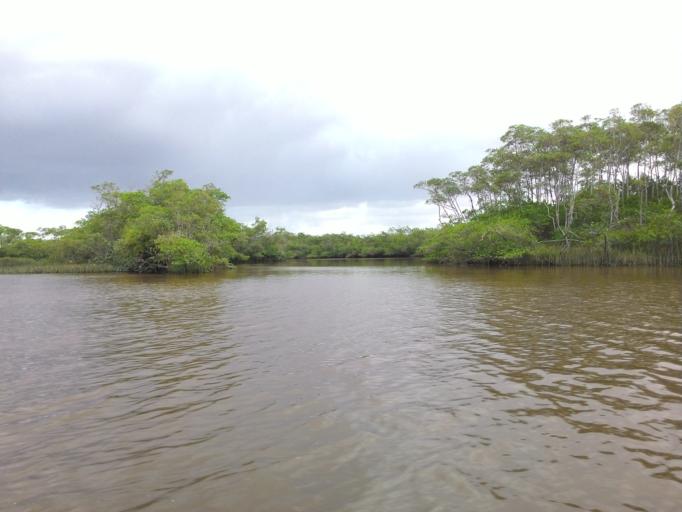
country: BR
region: Sao Paulo
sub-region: Pariquera-Acu
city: Pariquera Acu
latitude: -24.8227
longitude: -47.7360
